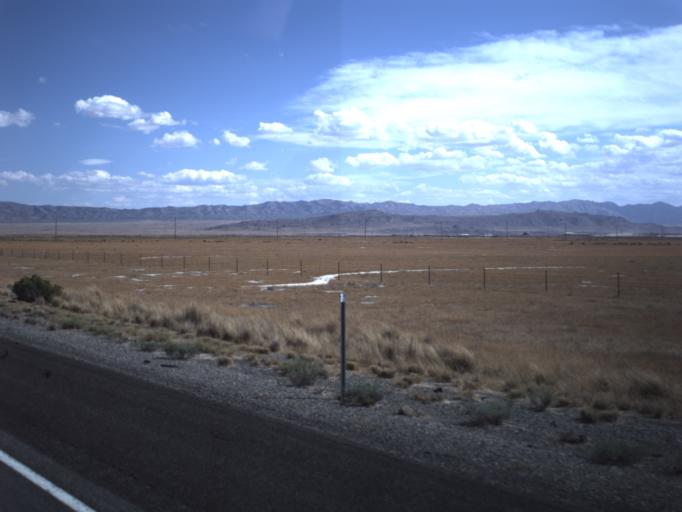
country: US
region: Utah
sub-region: Tooele County
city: Grantsville
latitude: 40.7251
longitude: -113.1505
